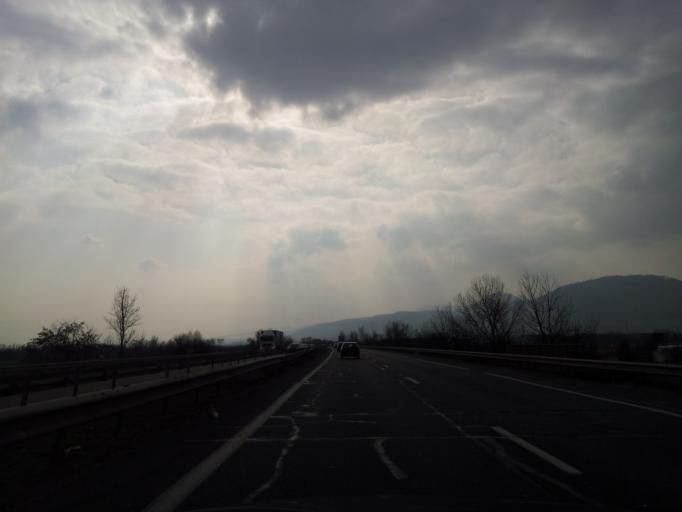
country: FR
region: Alsace
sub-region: Departement du Bas-Rhin
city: Selestat
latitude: 48.2757
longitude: 7.4356
